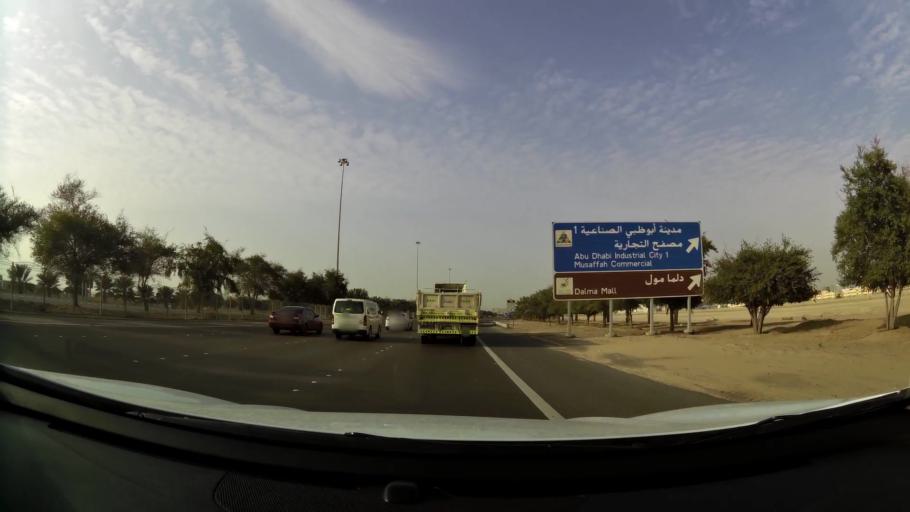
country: AE
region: Abu Dhabi
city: Abu Dhabi
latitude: 24.3143
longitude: 54.5269
